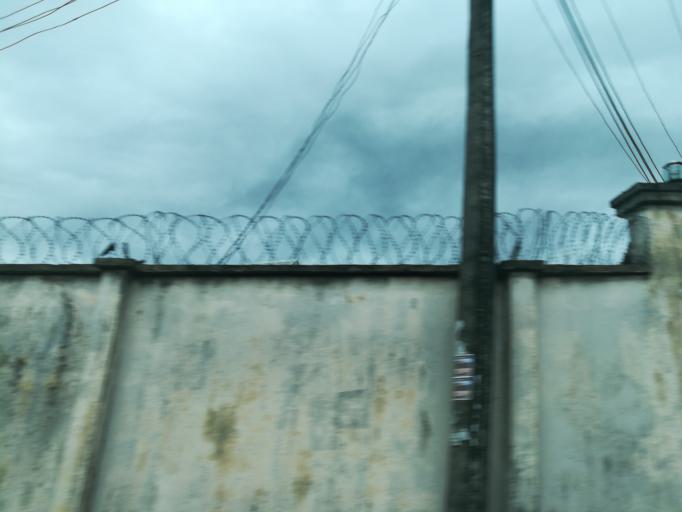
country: NG
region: Rivers
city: Port Harcourt
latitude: 4.8386
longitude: 7.0326
